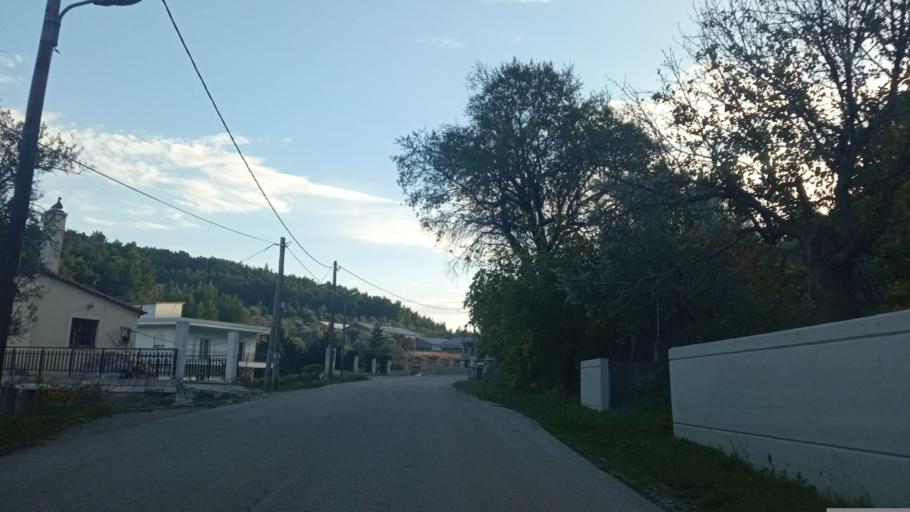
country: GR
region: Central Greece
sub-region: Nomos Evvoias
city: Psachna
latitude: 38.6143
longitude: 23.7317
